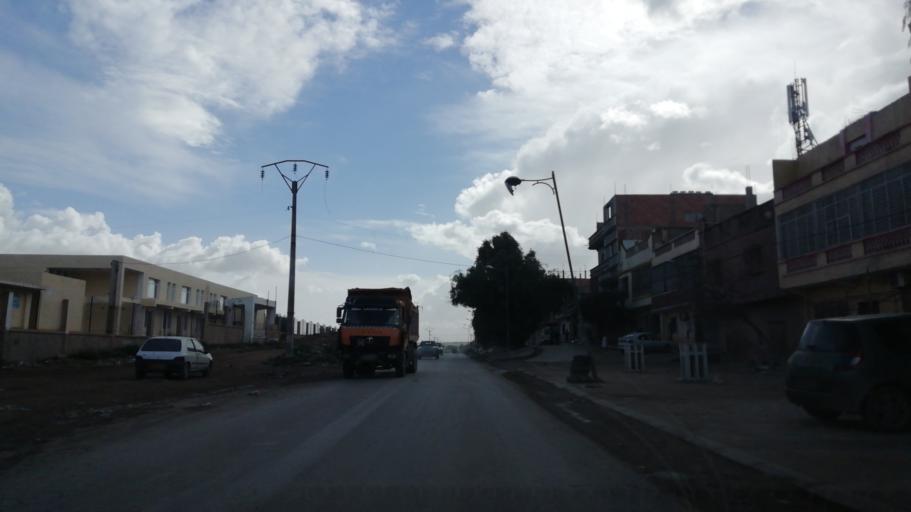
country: DZ
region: Oran
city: Sidi ech Chahmi
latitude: 35.6483
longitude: -0.5622
